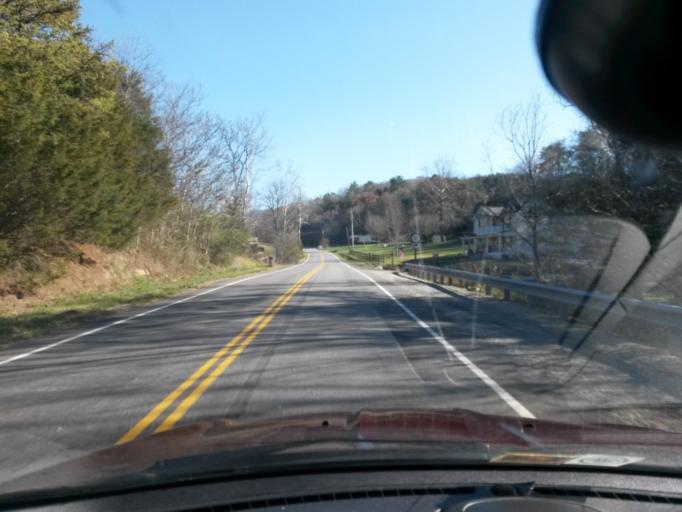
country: US
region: Virginia
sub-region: Botetourt County
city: Buchanan
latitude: 37.6415
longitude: -79.7748
